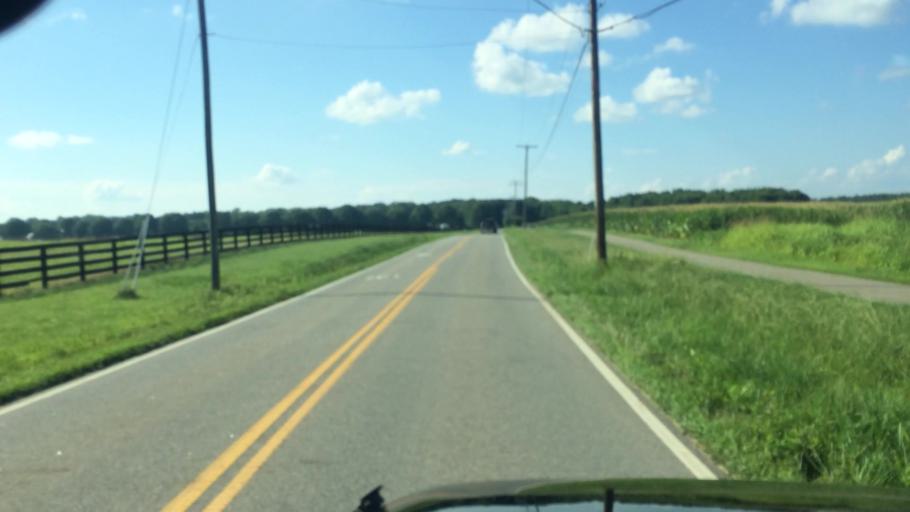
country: US
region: Virginia
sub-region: James City County
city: Williamsburg
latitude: 37.2321
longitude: -76.7836
